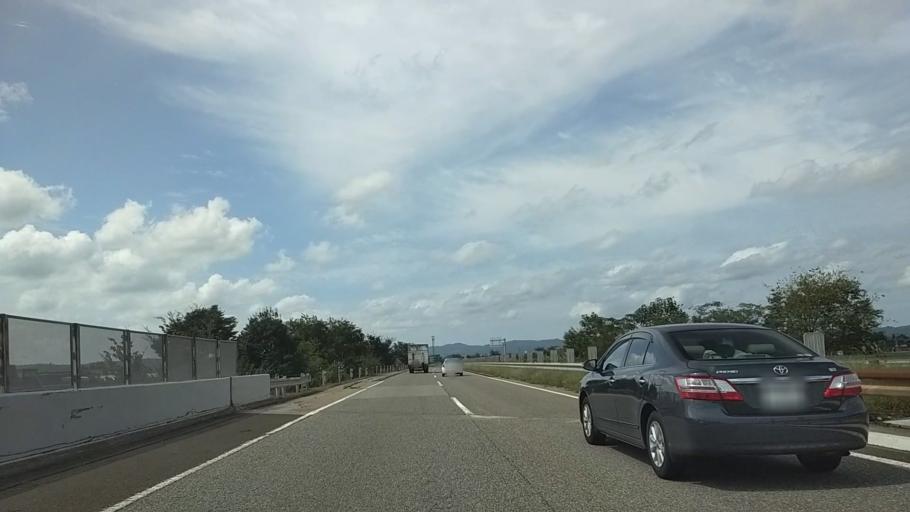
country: JP
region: Toyama
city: Nanto-shi
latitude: 36.6228
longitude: 136.9427
